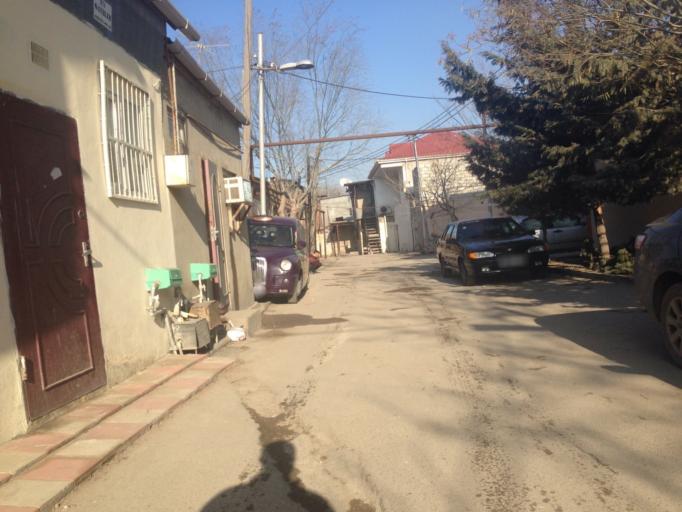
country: AZ
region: Baki
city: Baku
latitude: 40.3929
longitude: 49.8803
